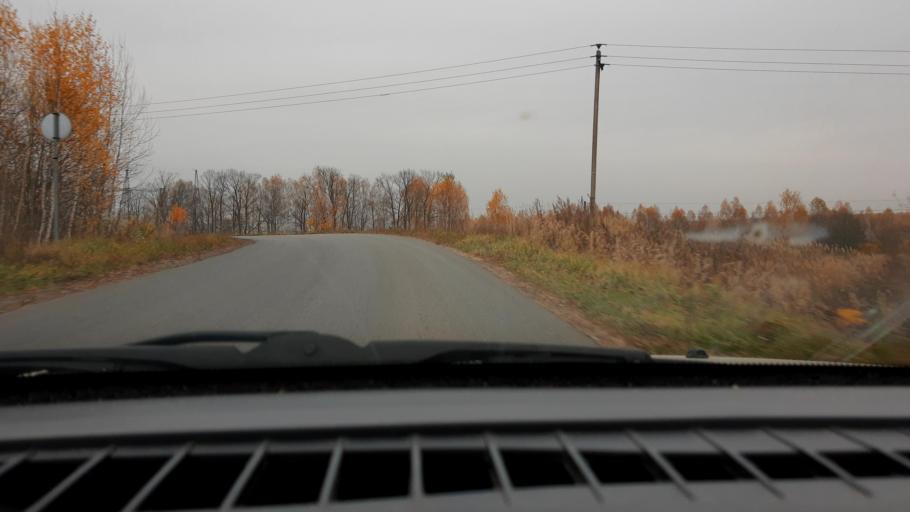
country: RU
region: Nizjnij Novgorod
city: Burevestnik
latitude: 56.0382
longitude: 43.8420
